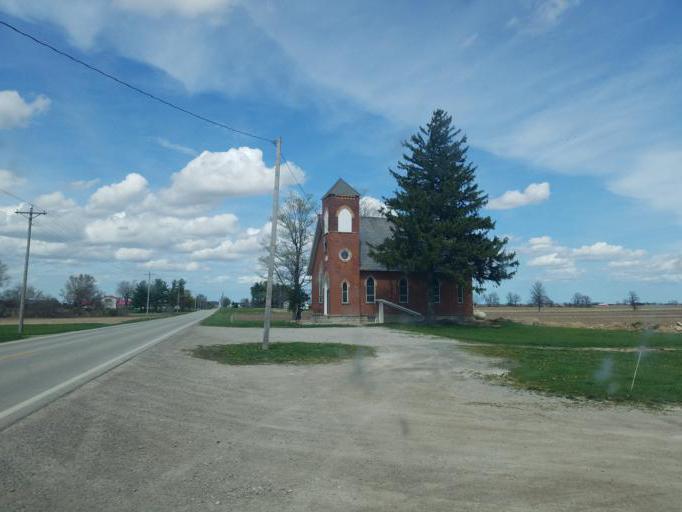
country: US
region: Ohio
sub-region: Huron County
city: Bellevue
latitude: 41.2213
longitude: -82.8147
